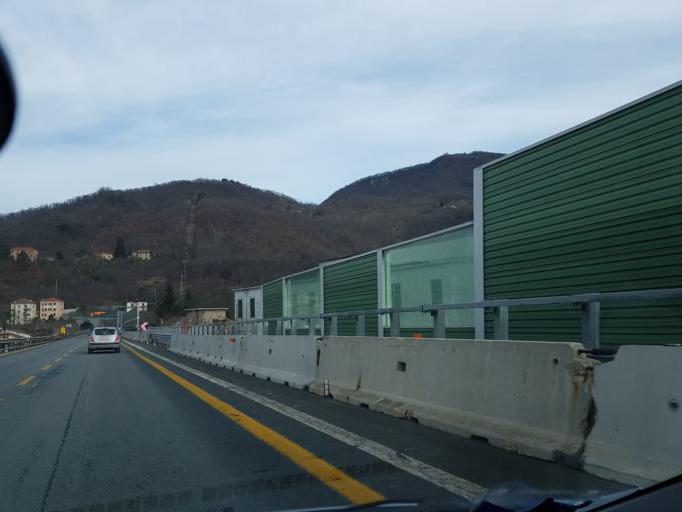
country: IT
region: Liguria
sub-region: Provincia di Genova
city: Ronco Scrivia
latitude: 44.6112
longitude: 8.9568
